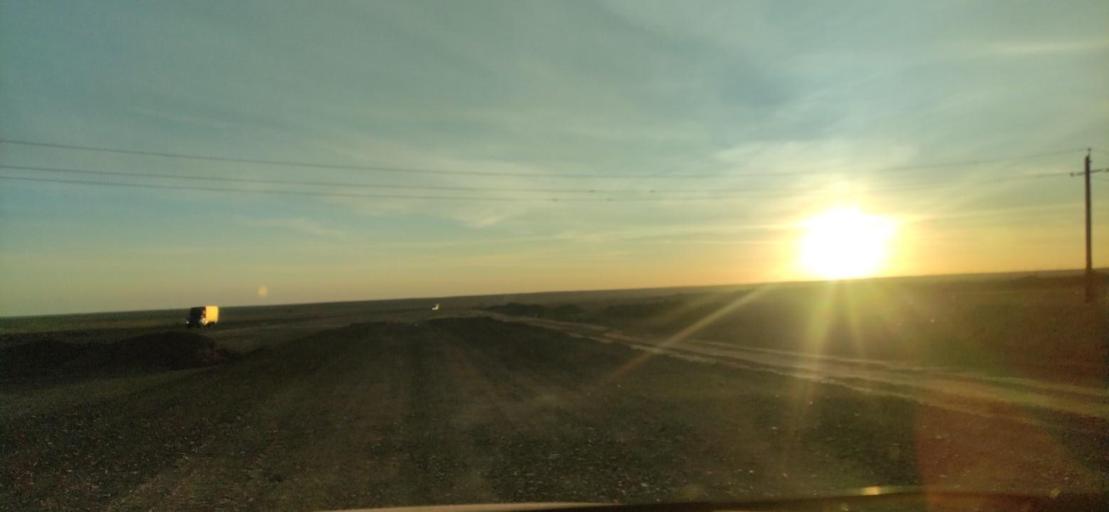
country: KZ
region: Qaraghandy
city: Saryshaghan
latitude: 46.0071
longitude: 73.5854
